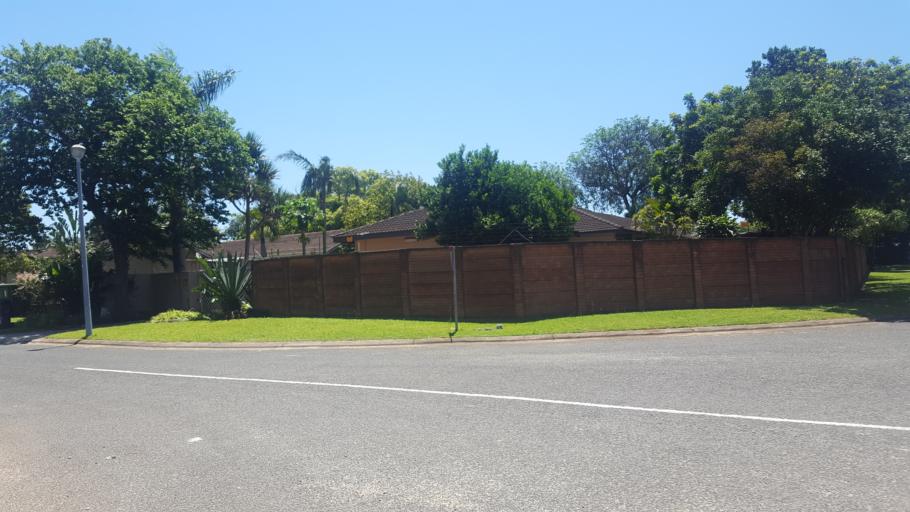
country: ZA
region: KwaZulu-Natal
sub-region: uThungulu District Municipality
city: Richards Bay
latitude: -28.7632
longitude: 32.0702
